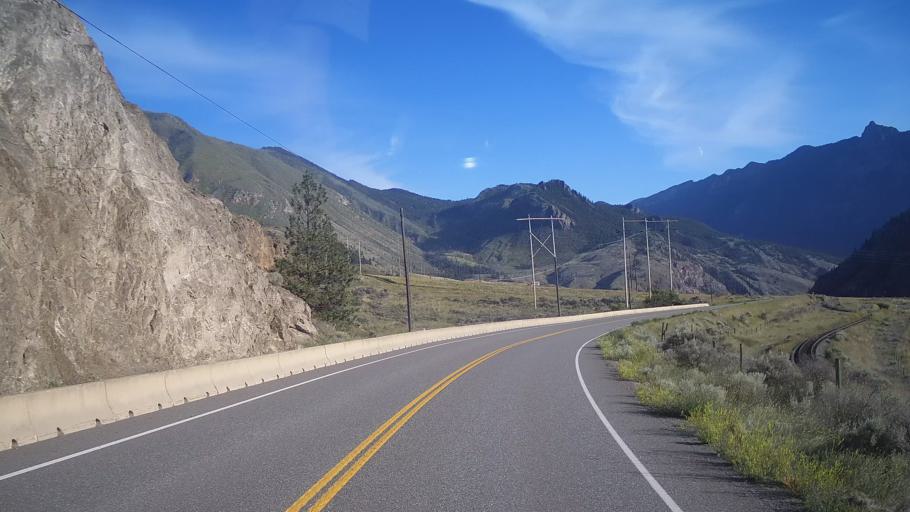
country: CA
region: British Columbia
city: Lillooet
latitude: 50.7769
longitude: -121.8385
